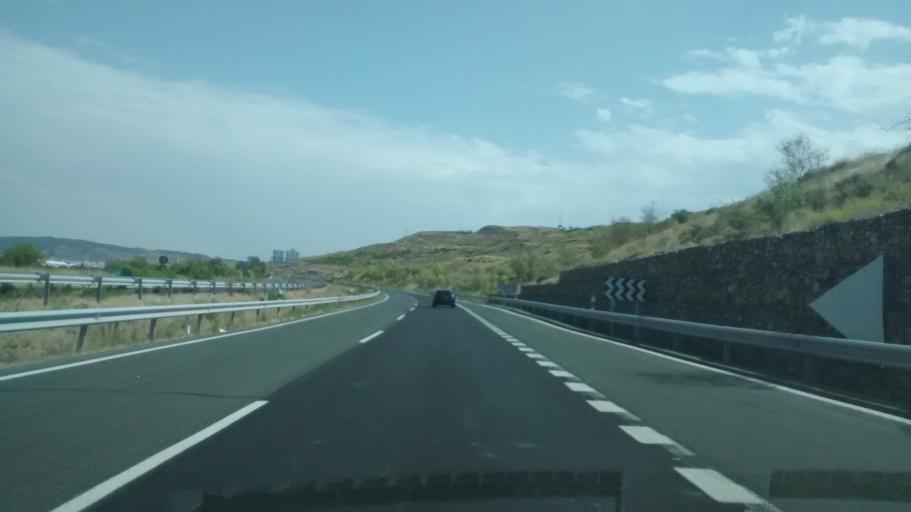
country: ES
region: La Rioja
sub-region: Provincia de La Rioja
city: Agoncillo
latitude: 42.4344
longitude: -2.2892
